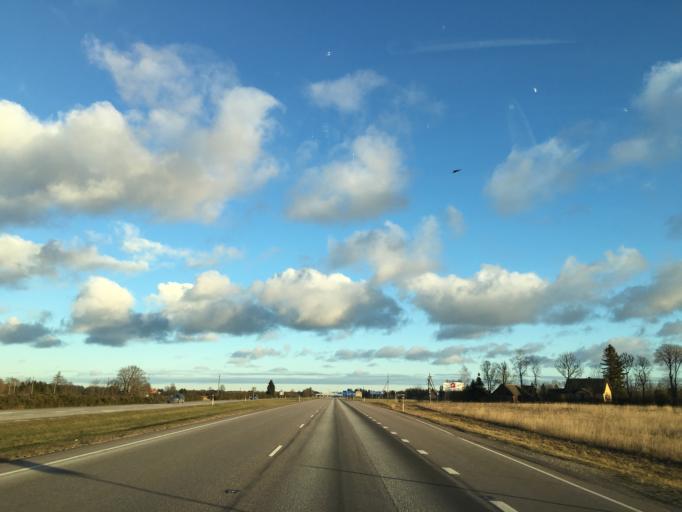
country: EE
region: Harju
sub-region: Saue linn
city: Saue
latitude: 59.3023
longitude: 24.5595
